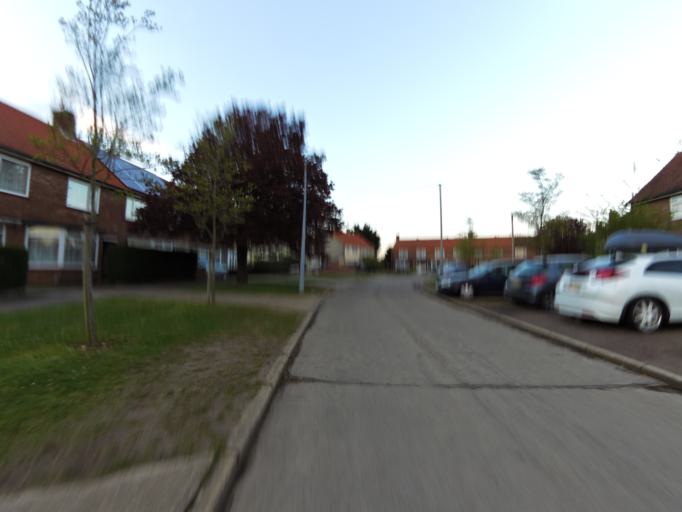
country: GB
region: England
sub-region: Suffolk
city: Ipswich
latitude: 52.0721
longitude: 1.1899
